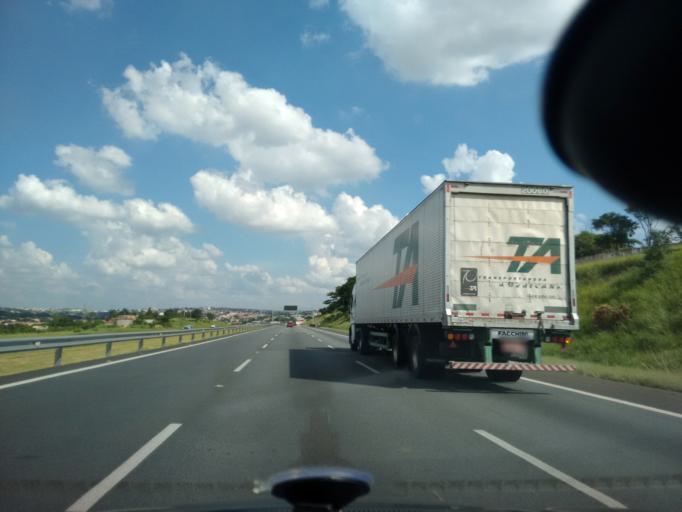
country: BR
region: Sao Paulo
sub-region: Campinas
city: Campinas
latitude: -22.9494
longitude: -47.1261
